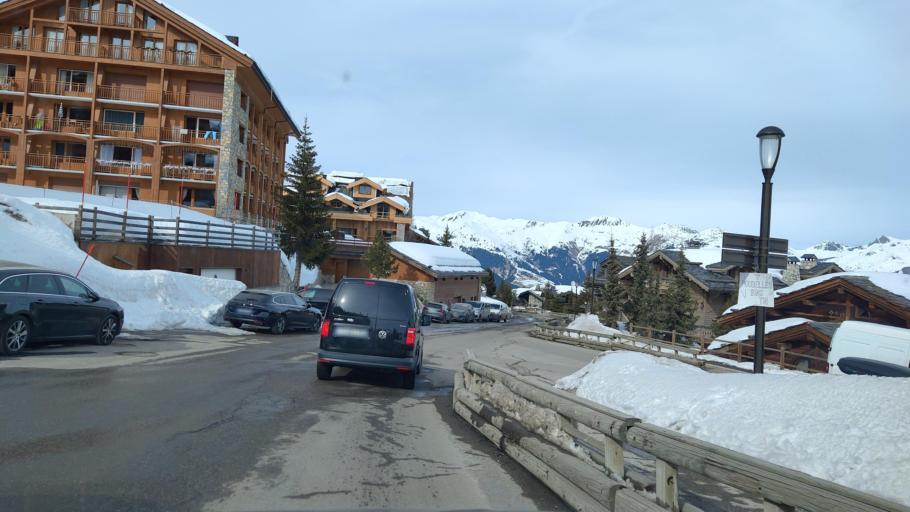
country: FR
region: Rhone-Alpes
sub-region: Departement de la Savoie
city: Courchevel
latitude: 45.4078
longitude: 6.6367
